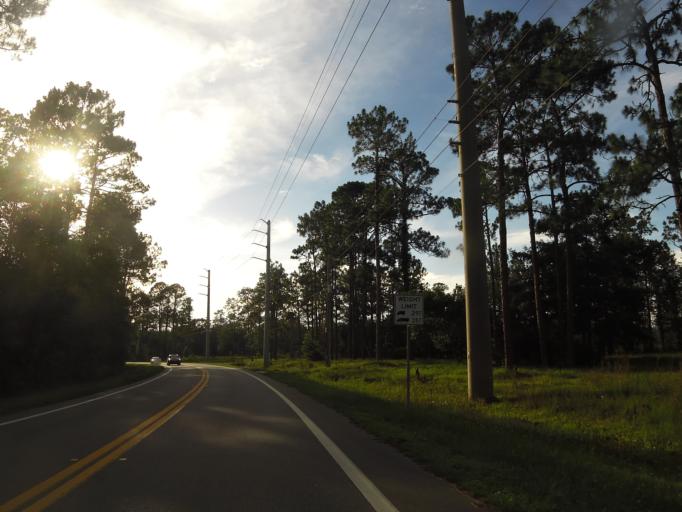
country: US
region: Florida
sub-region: Clay County
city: Green Cove Springs
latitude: 30.0144
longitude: -81.5602
